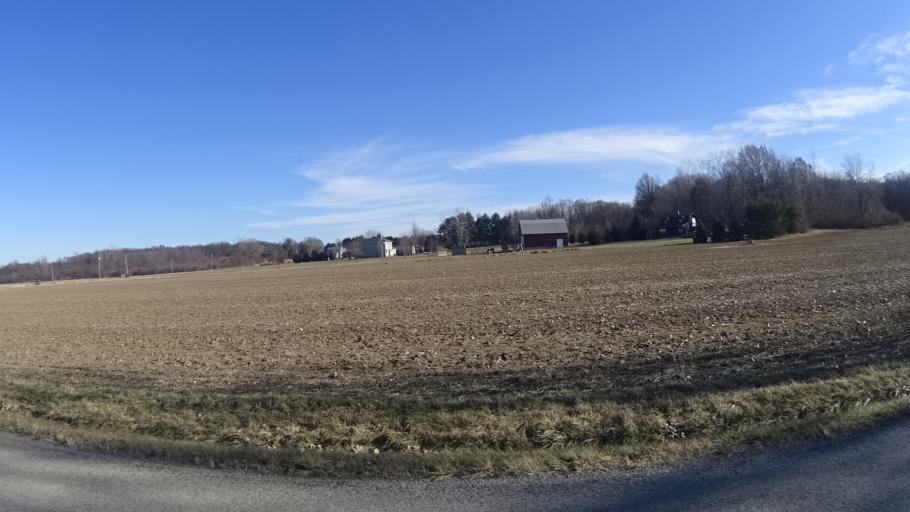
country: US
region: Ohio
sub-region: Lorain County
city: South Amherst
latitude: 41.3130
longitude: -82.2877
